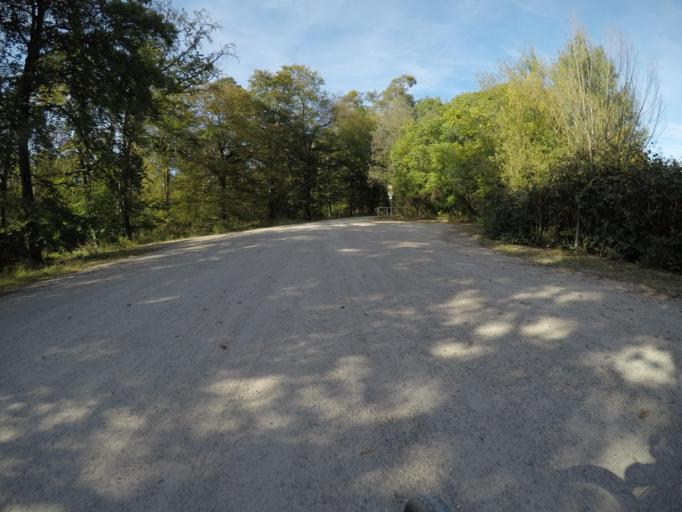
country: DE
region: Baden-Wuerttemberg
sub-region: Karlsruhe Region
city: Kronau
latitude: 49.2380
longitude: 8.6096
